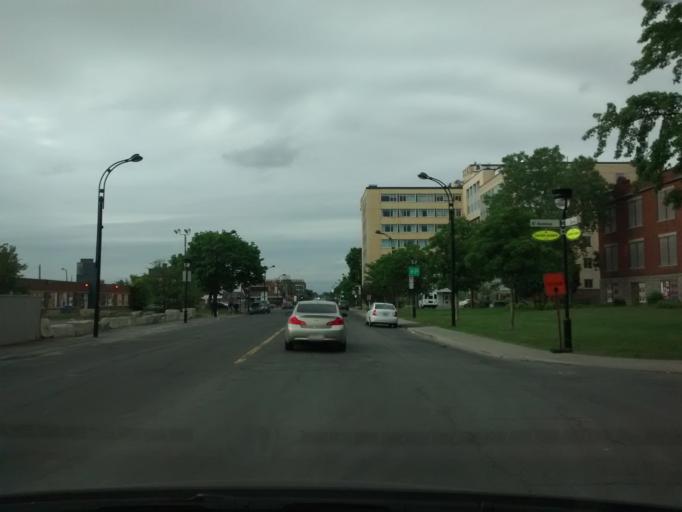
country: CA
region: Quebec
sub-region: Montreal
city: Saint-Leonard
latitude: 45.5613
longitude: -73.6119
